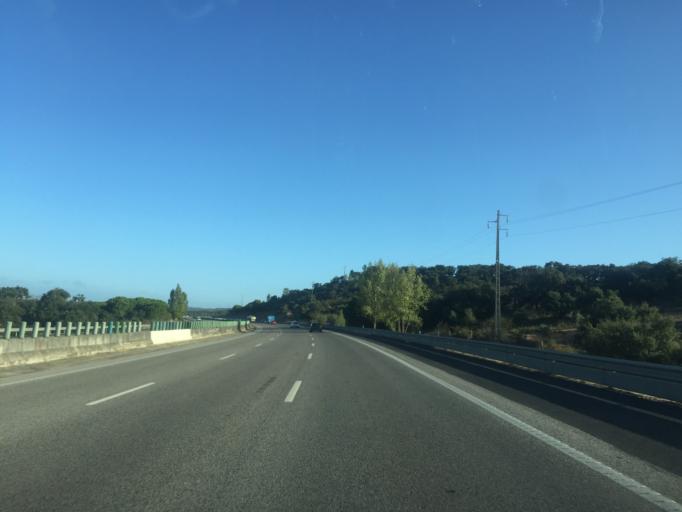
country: PT
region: Lisbon
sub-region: Alenquer
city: Carregado
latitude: 39.0538
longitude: -8.9426
